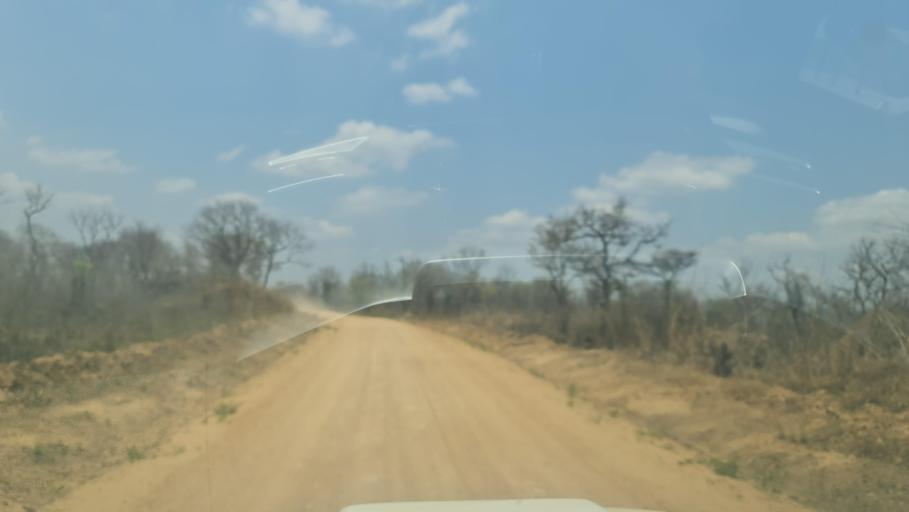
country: MW
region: Southern Region
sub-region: Nsanje District
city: Nsanje
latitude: -17.5694
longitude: 35.9040
